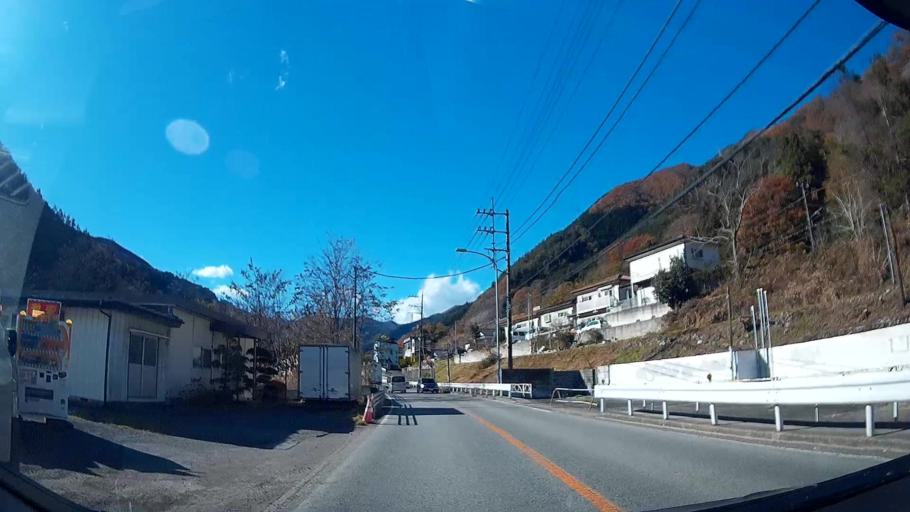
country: JP
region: Yamanashi
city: Otsuki
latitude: 35.6051
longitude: 138.8373
